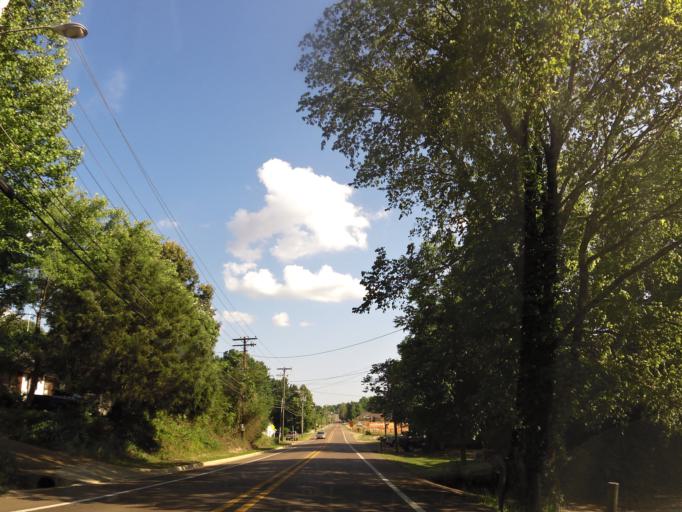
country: US
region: Mississippi
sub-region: Lafayette County
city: University
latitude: 34.3443
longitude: -89.5210
